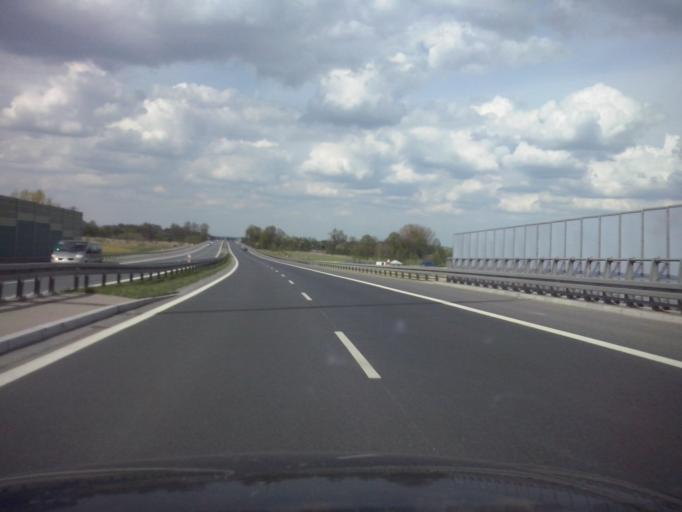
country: PL
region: Subcarpathian Voivodeship
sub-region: Powiat rzeszowski
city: Trzebownisko
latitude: 50.0678
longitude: 22.0551
